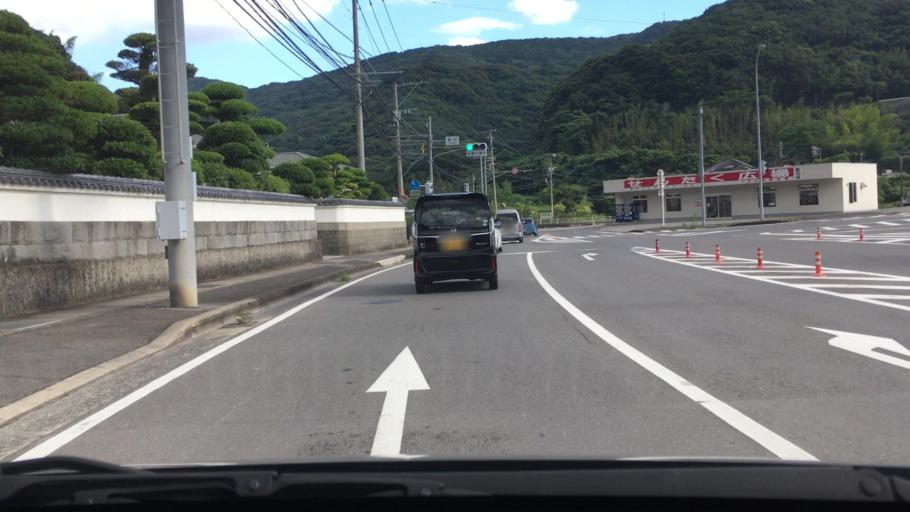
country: JP
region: Nagasaki
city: Togitsu
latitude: 32.8269
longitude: 129.7843
